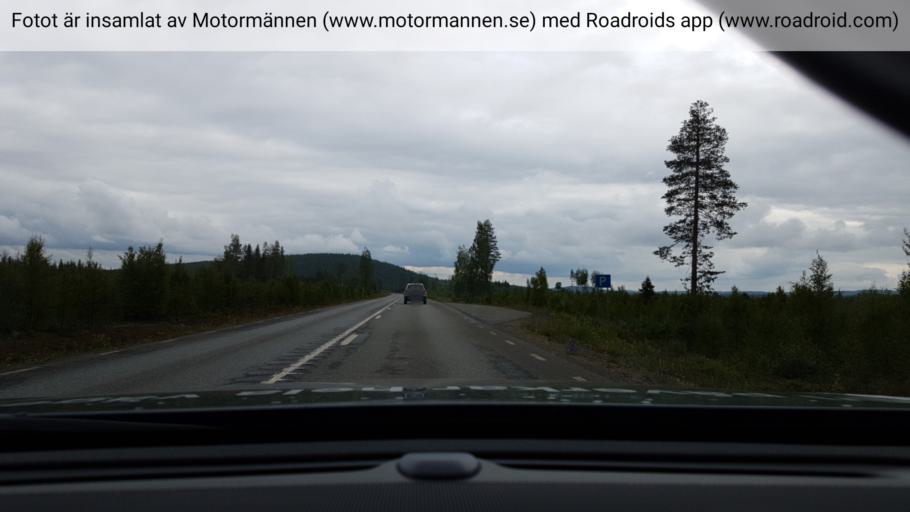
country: SE
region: Vaesterbotten
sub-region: Norsjo Kommun
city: Norsjoe
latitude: 65.1652
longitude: 19.8795
